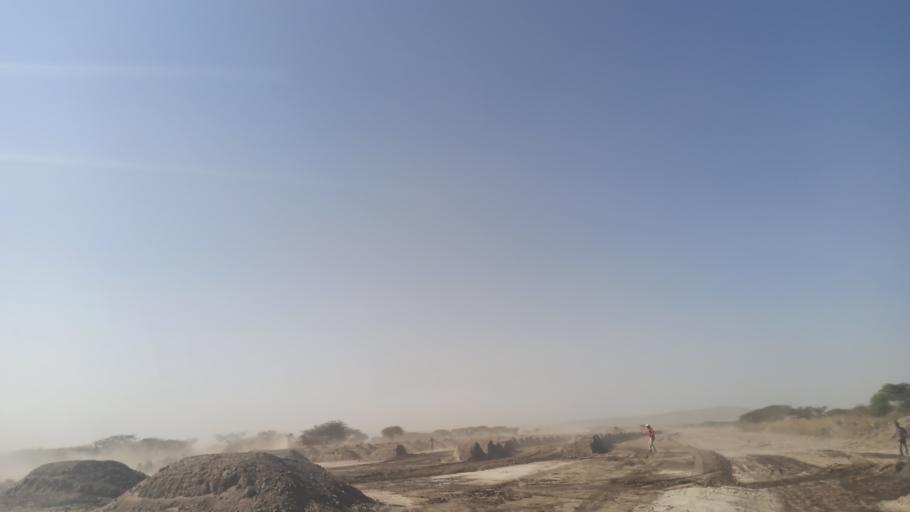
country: ET
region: Oromiya
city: Ziway
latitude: 7.7406
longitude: 38.6203
